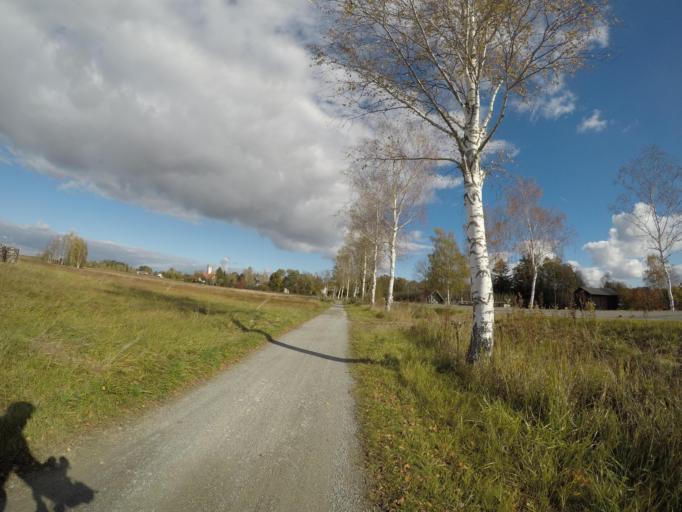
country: DE
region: Baden-Wuerttemberg
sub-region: Tuebingen Region
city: Oggelshausen
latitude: 48.0672
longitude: 9.6442
